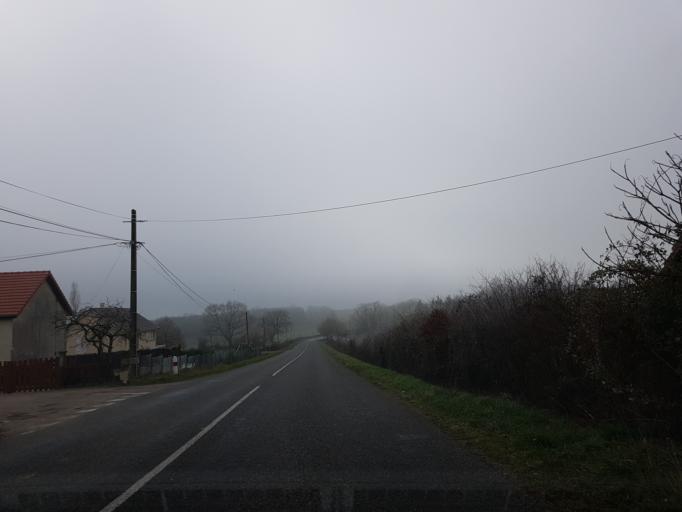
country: FR
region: Bourgogne
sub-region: Departement de Saone-et-Loire
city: Saint-Berain-sous-Sanvignes
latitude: 46.7173
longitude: 4.2635
